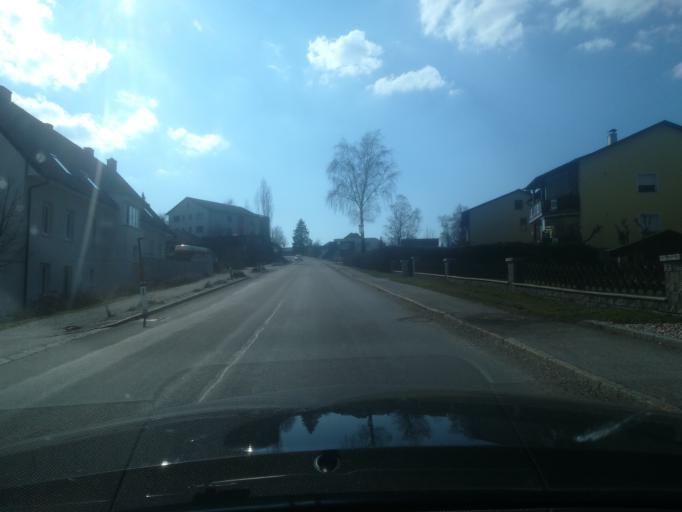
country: AT
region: Upper Austria
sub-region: Politischer Bezirk Freistadt
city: Freistadt
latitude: 48.4458
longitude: 14.6822
